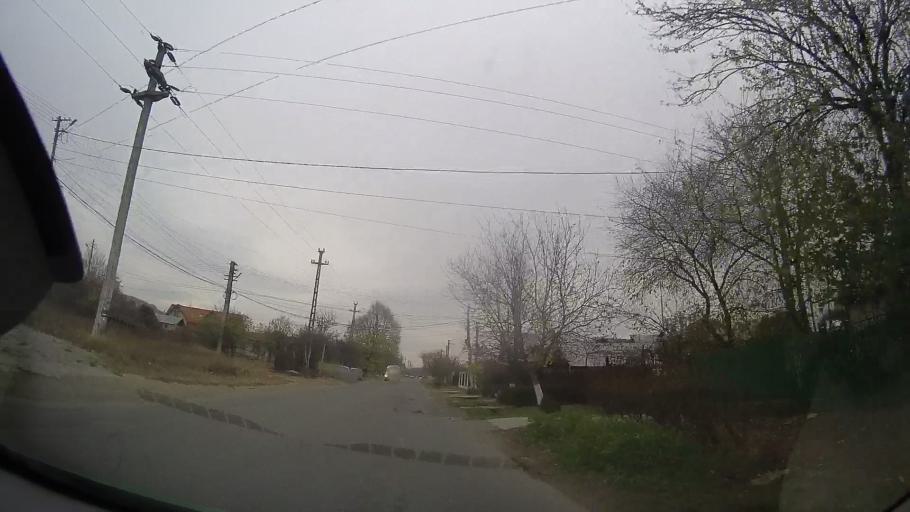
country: RO
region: Prahova
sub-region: Oras Urlati
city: Urlati
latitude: 45.0019
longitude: 26.2273
